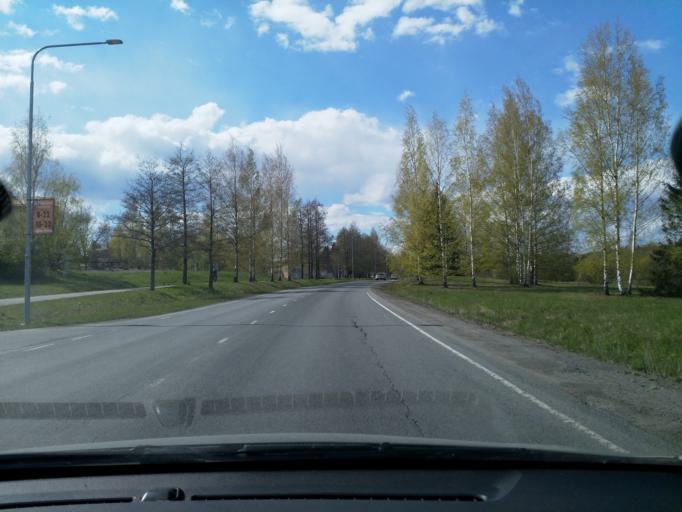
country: FI
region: Pirkanmaa
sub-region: Tampere
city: Tampere
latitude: 61.4804
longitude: 23.8114
